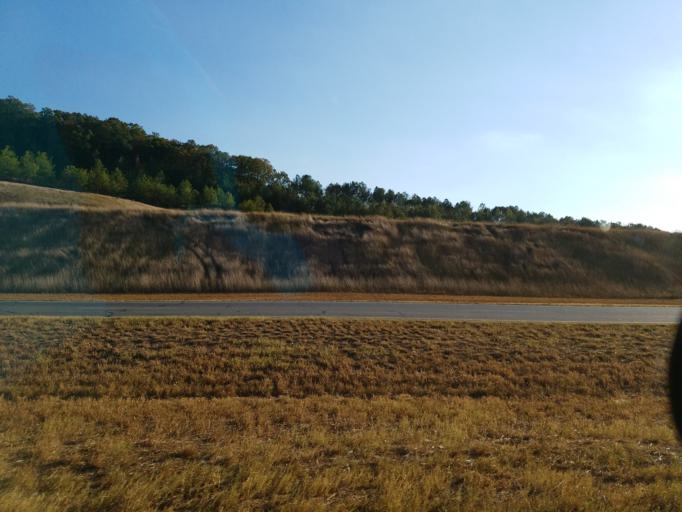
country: US
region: Georgia
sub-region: Bartow County
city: Cartersville
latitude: 34.2182
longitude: -84.8681
